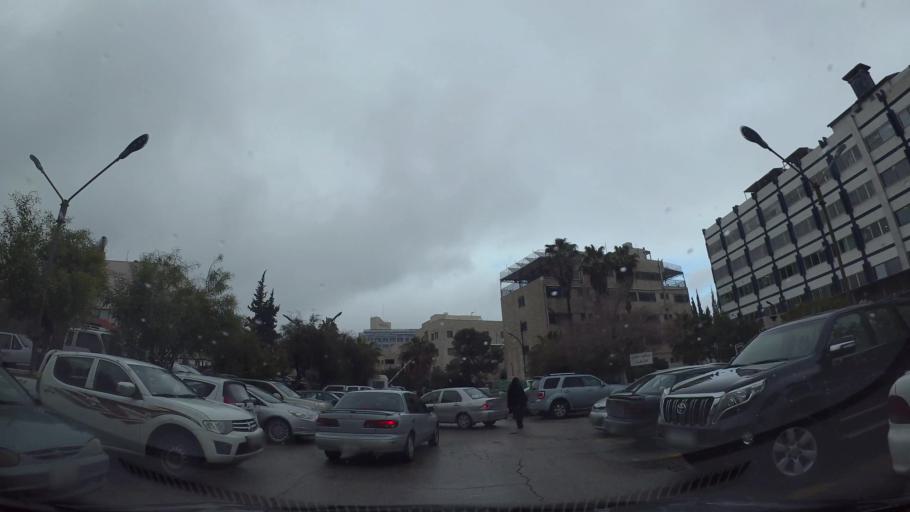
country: JO
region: Amman
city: Amman
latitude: 31.9667
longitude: 35.9071
